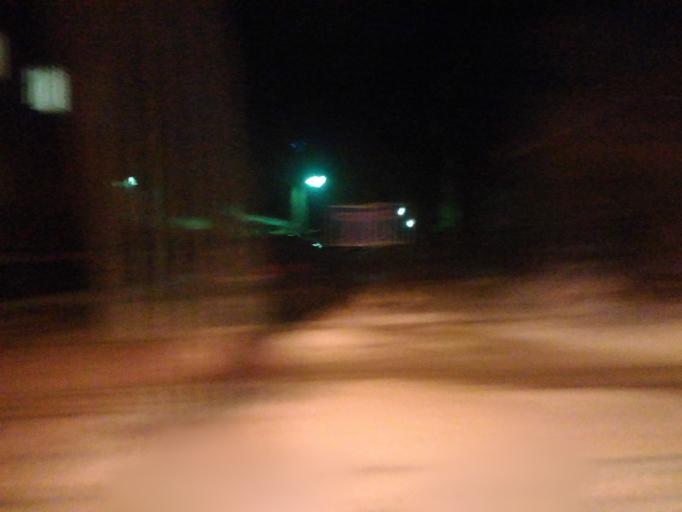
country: RU
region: Ulyanovsk
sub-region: Ulyanovskiy Rayon
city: Ulyanovsk
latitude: 54.3307
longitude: 48.4012
